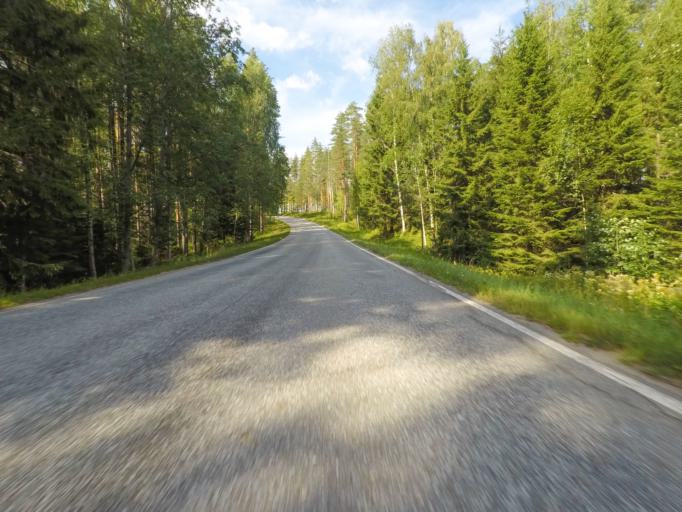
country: FI
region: Southern Savonia
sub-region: Mikkeli
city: Puumala
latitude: 61.6947
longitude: 28.2158
